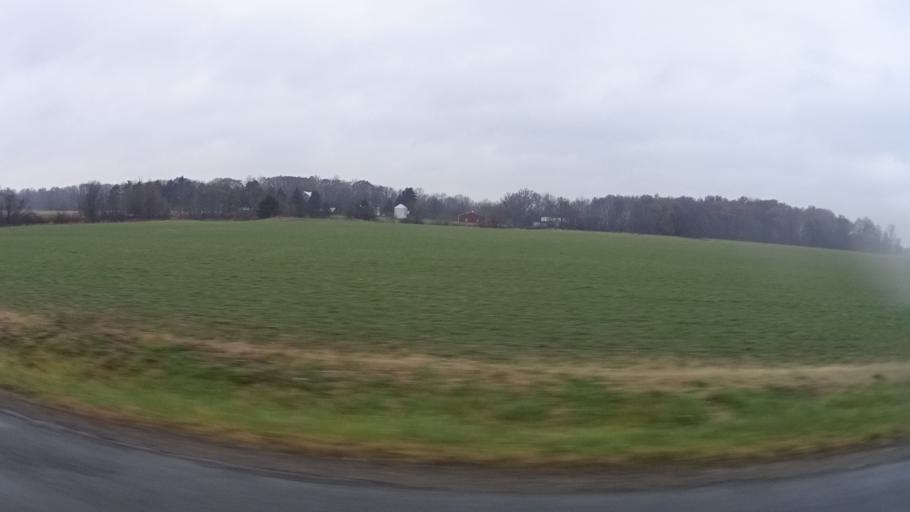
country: US
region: Ohio
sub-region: Lorain County
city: Lagrange
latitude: 41.2747
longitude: -82.1512
